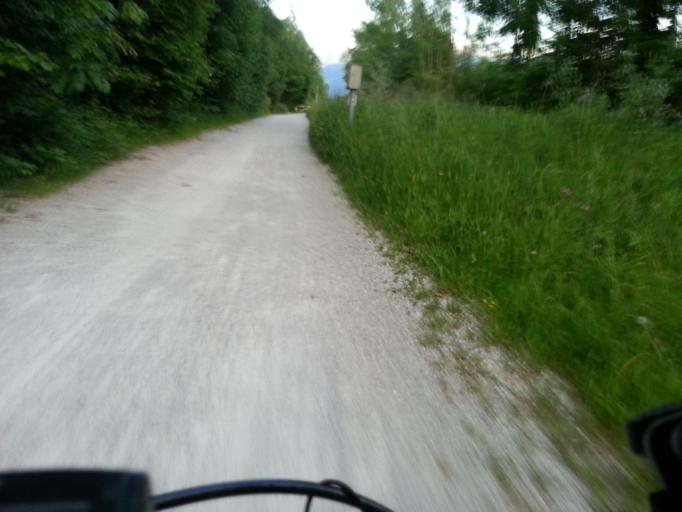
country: AT
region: Salzburg
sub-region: Politischer Bezirk Salzburg-Umgebung
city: Elsbethen
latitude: 47.7431
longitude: 13.0819
